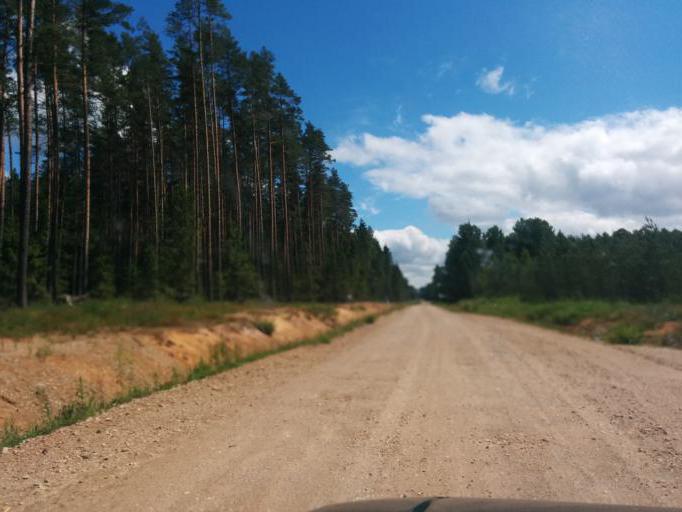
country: LV
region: Vilaka
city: Vilaka
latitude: 57.3216
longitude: 27.6820
